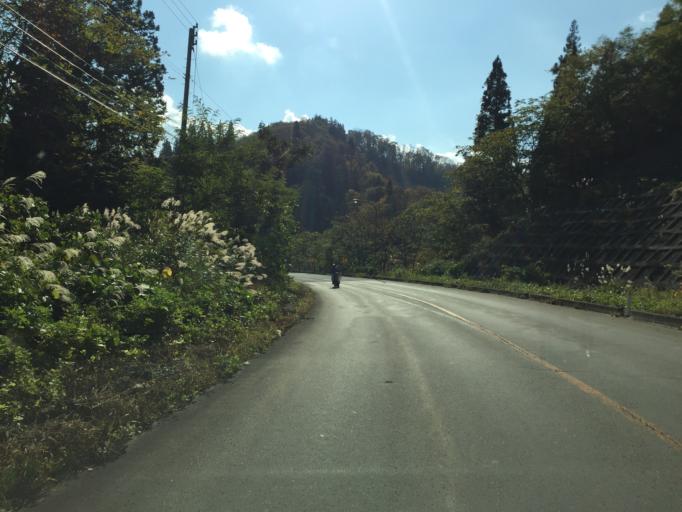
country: JP
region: Yamagata
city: Yonezawa
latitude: 37.8810
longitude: 139.9846
